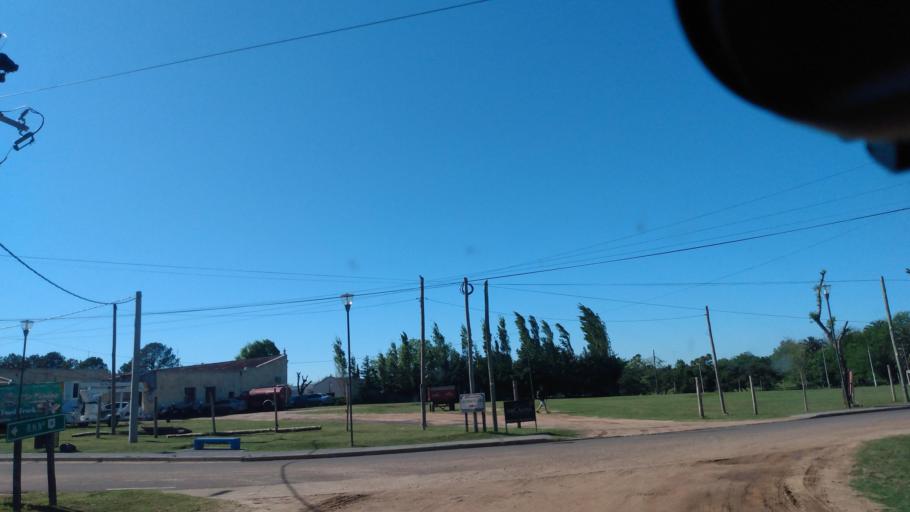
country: AR
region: Entre Rios
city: Colon
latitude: -32.1547
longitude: -58.1955
